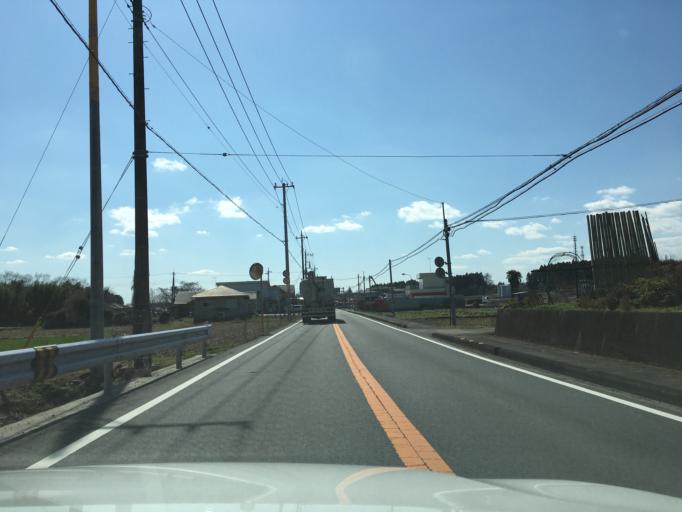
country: JP
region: Tochigi
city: Otawara
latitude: 36.8740
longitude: 140.1195
